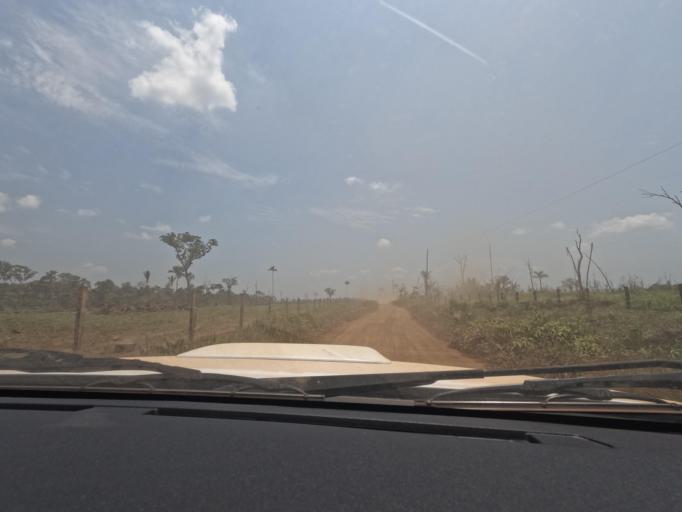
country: BR
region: Rondonia
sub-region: Porto Velho
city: Porto Velho
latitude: -8.6483
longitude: -64.1719
